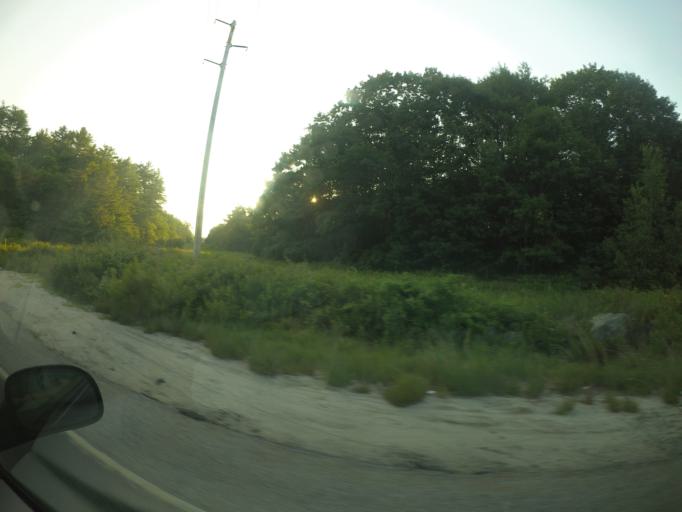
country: US
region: Maine
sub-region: Cumberland County
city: Raymond
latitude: 43.8950
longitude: -70.4571
